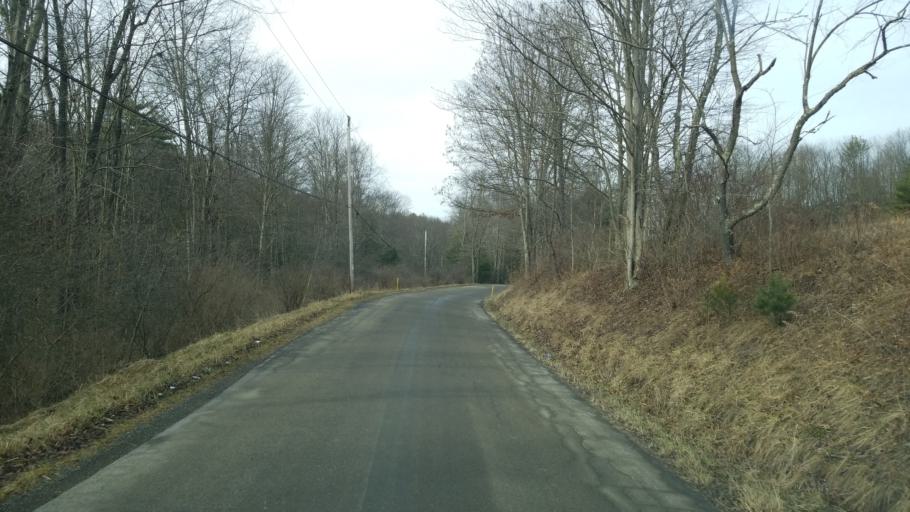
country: US
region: Pennsylvania
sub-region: Jefferson County
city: Punxsutawney
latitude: 40.8438
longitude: -78.9986
